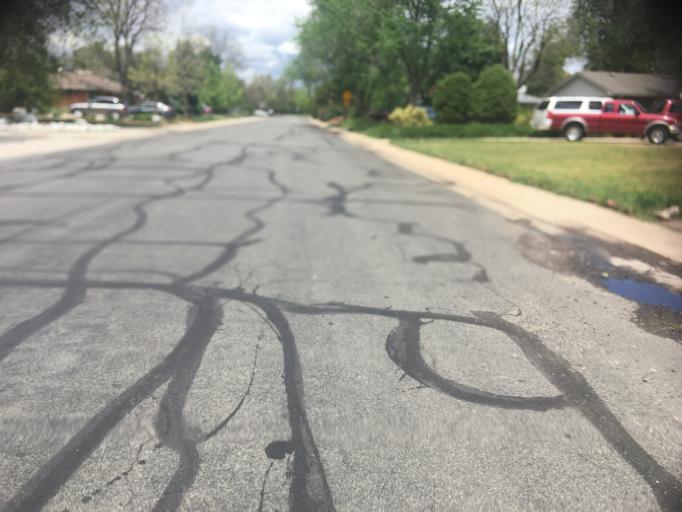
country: US
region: Colorado
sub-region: Boulder County
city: Boulder
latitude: 40.0023
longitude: -105.2305
